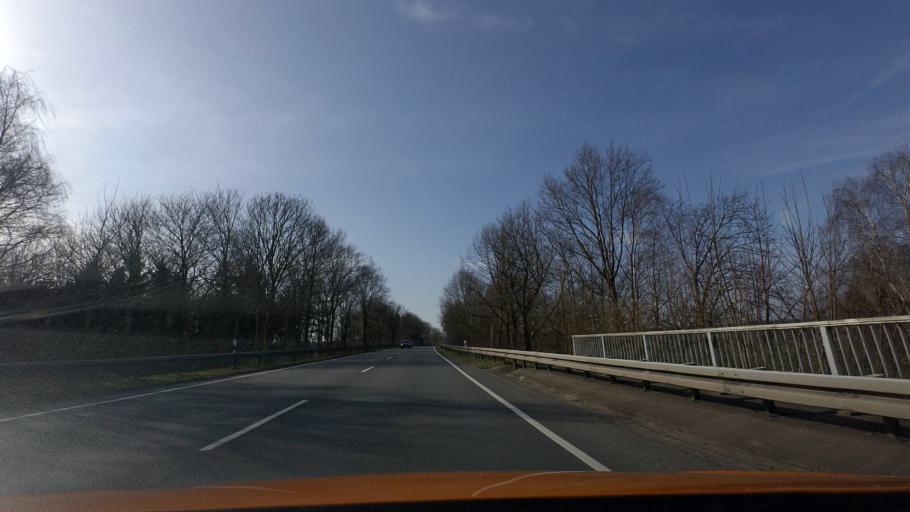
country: DE
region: Lower Saxony
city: Uchte
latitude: 52.5038
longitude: 8.9005
